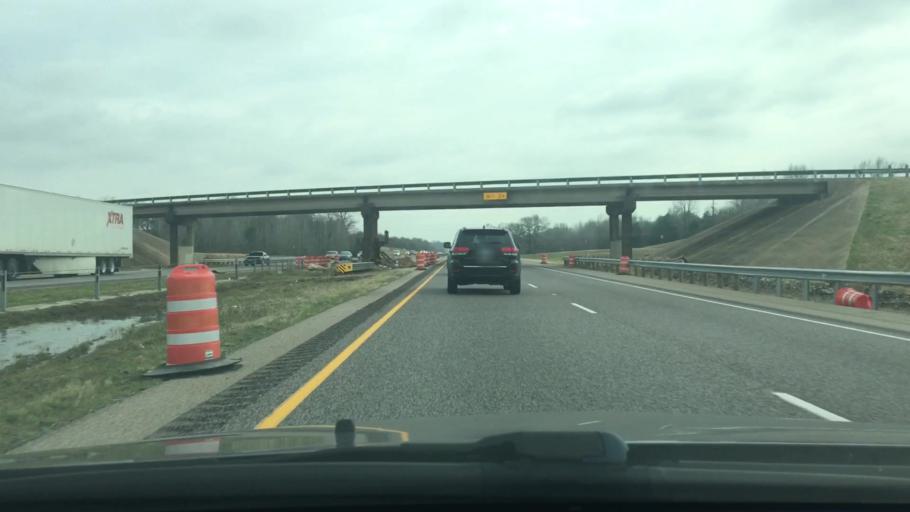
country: US
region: Texas
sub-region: Leon County
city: Buffalo
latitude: 31.5006
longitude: -96.0975
